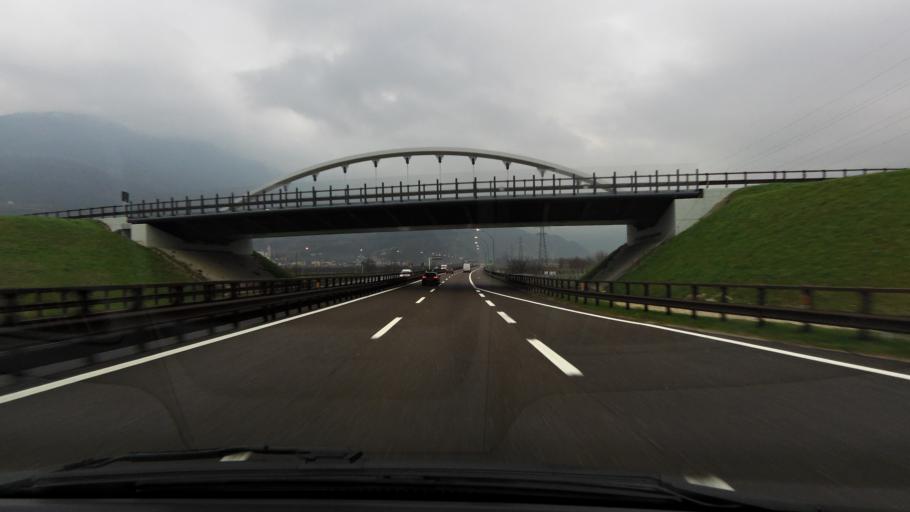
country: IT
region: Trentino-Alto Adige
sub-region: Provincia di Trento
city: Villa Lagarina
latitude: 45.9162
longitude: 11.0388
